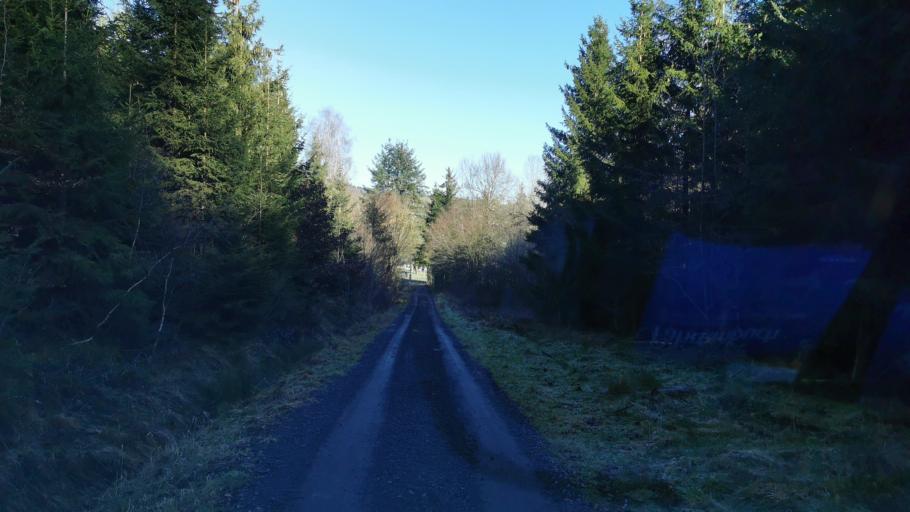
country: DE
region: Rheinland-Pfalz
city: Weidenbach
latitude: 50.1254
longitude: 6.7027
